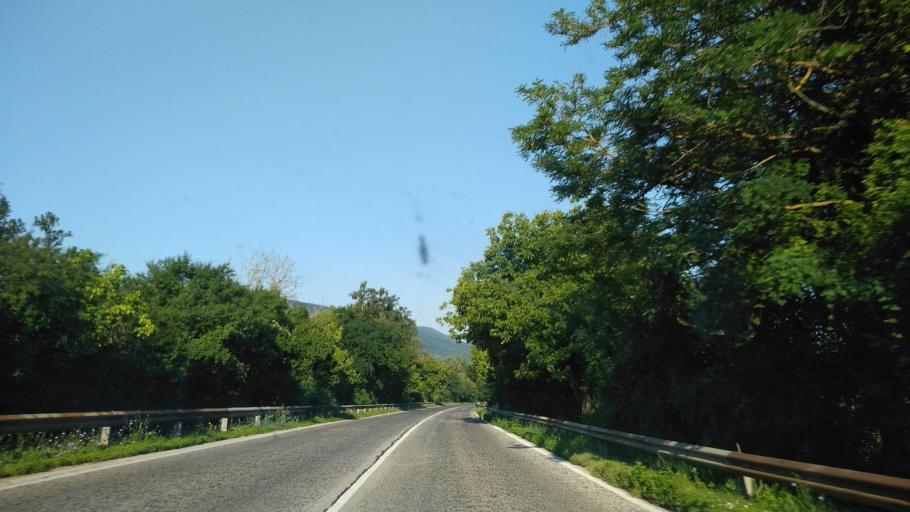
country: BG
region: Lovech
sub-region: Obshtina Lovech
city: Lovech
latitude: 43.0409
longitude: 24.7351
